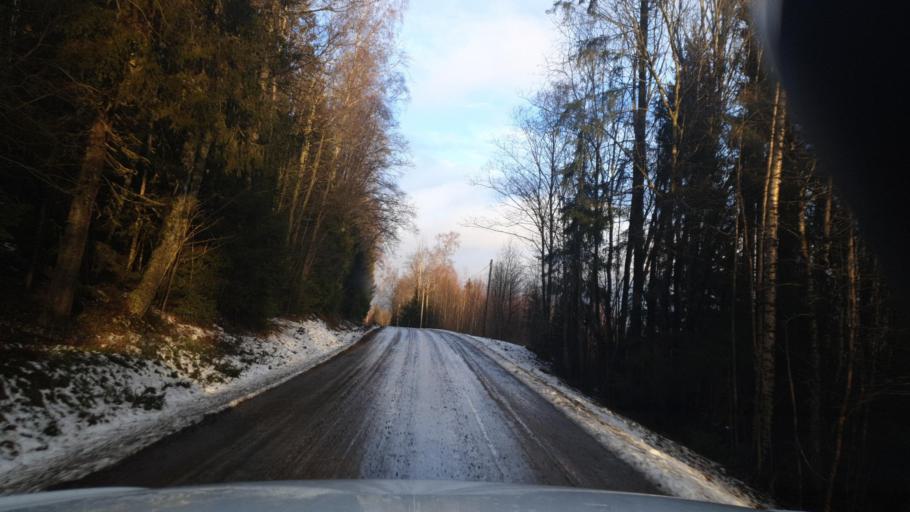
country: SE
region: Vaermland
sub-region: Eda Kommun
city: Amotfors
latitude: 59.7393
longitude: 12.2777
